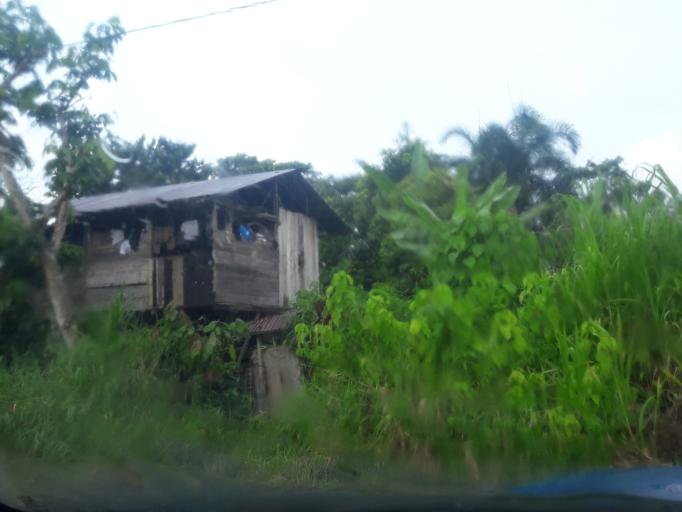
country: EC
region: Napo
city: Tena
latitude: -0.9893
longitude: -77.8068
